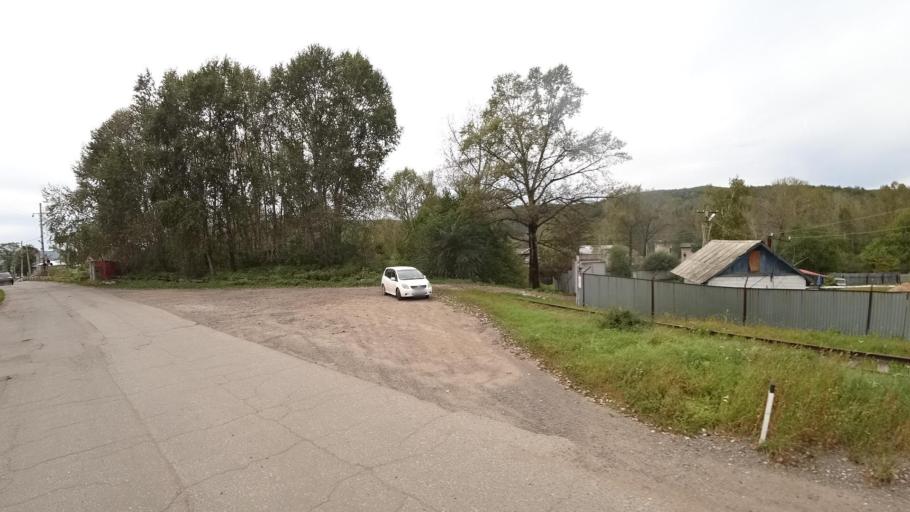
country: RU
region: Jewish Autonomous Oblast
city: Khingansk
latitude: 49.0186
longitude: 131.0546
